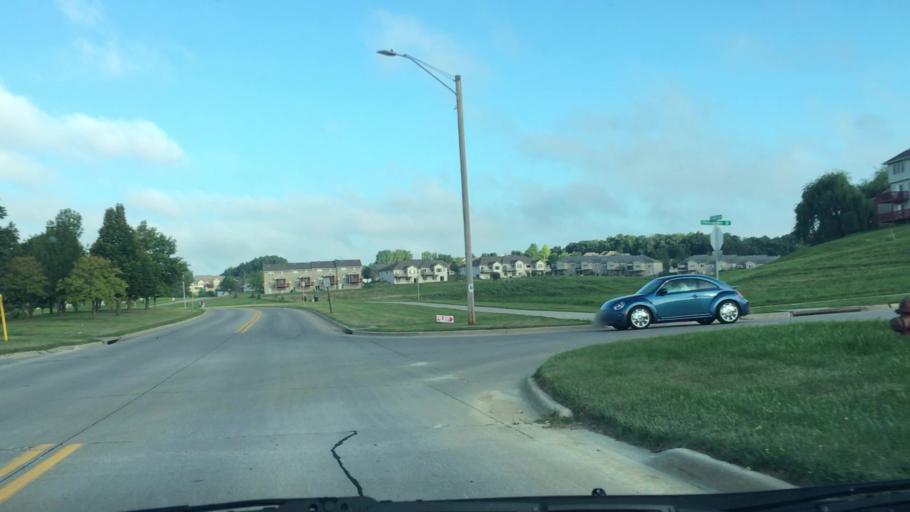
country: US
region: Iowa
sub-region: Johnson County
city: Coralville
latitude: 41.7021
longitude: -91.5555
